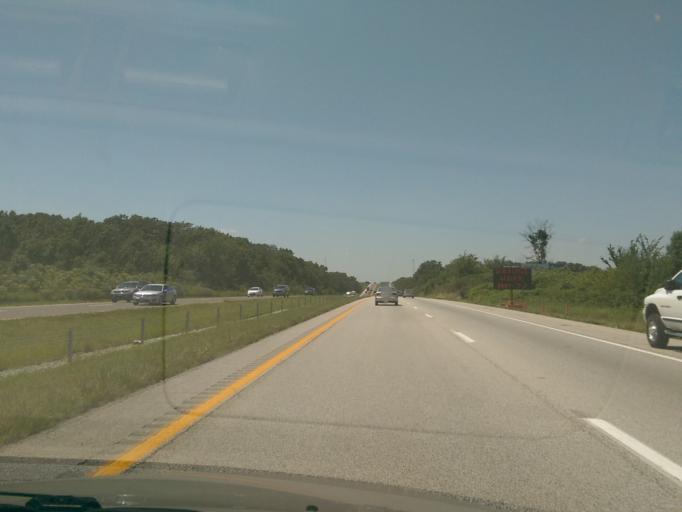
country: US
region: Missouri
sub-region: Saline County
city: Marshall
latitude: 38.9482
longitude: -93.0135
